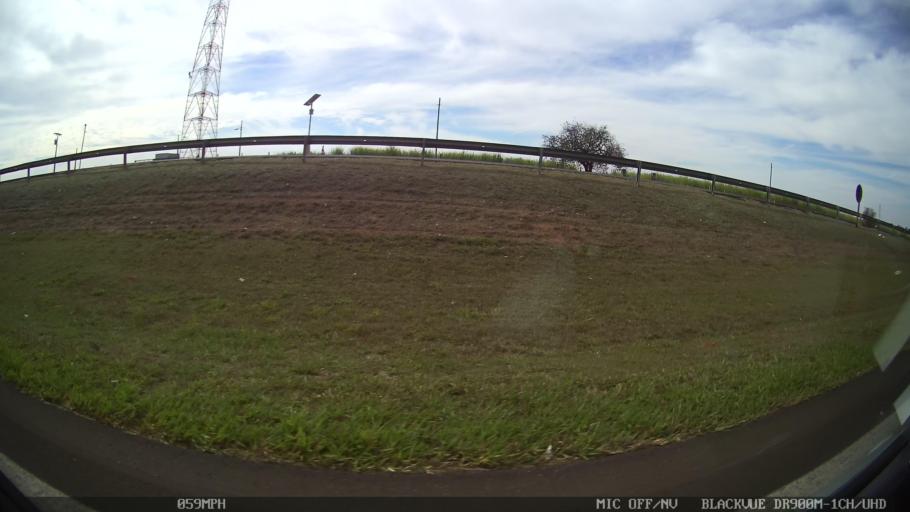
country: BR
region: Sao Paulo
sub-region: Matao
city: Matao
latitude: -21.5674
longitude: -48.4655
